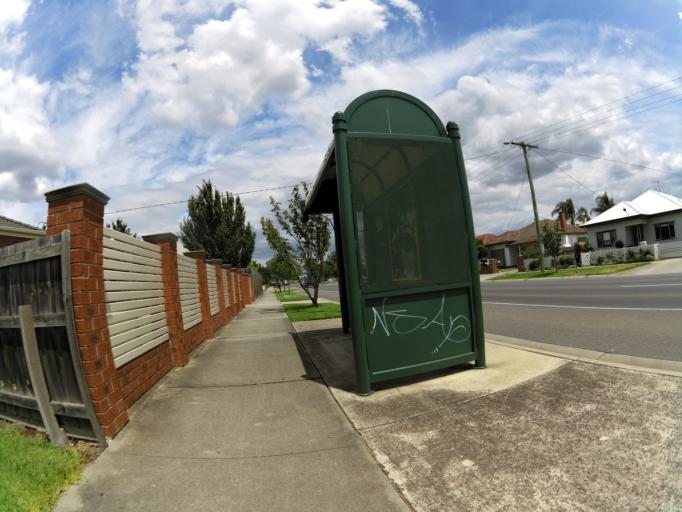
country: AU
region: Victoria
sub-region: Latrobe
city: Traralgon
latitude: -38.1915
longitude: 146.5340
